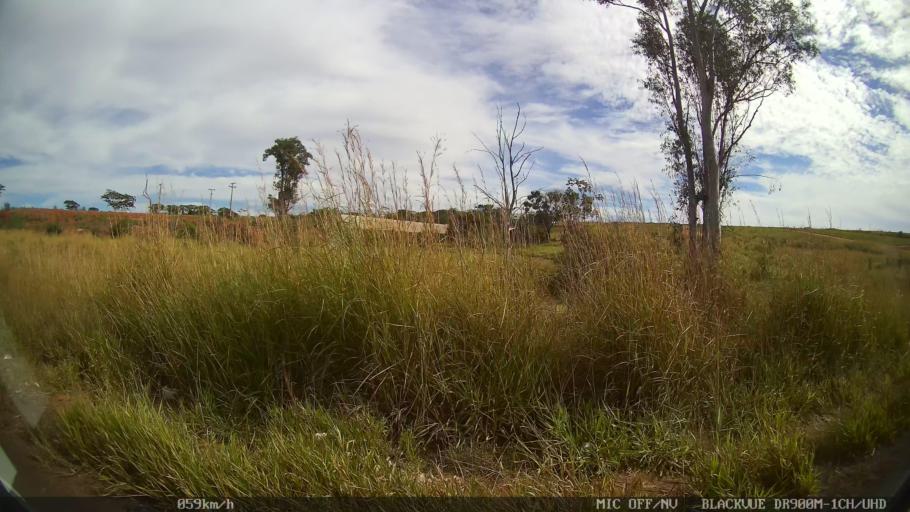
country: BR
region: Sao Paulo
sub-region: Catanduva
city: Catanduva
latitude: -21.1762
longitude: -48.9632
